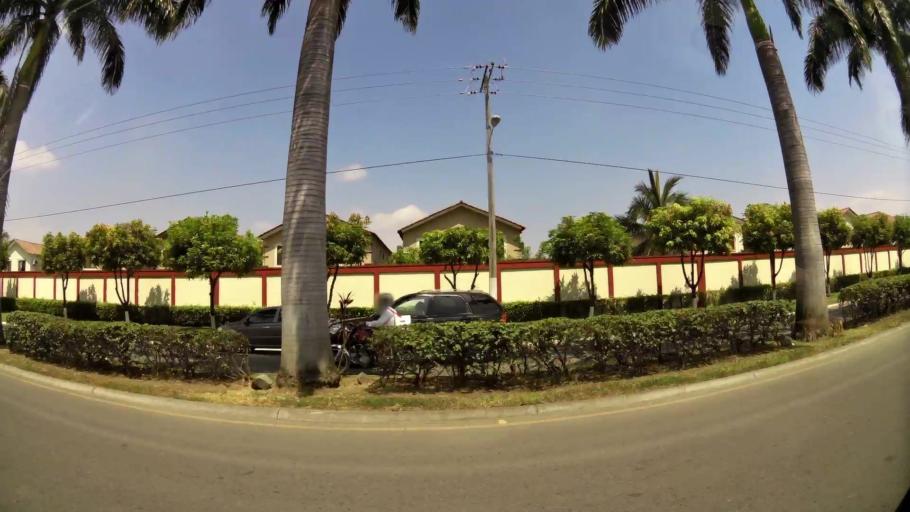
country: EC
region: Guayas
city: Eloy Alfaro
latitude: -2.0740
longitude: -79.8468
